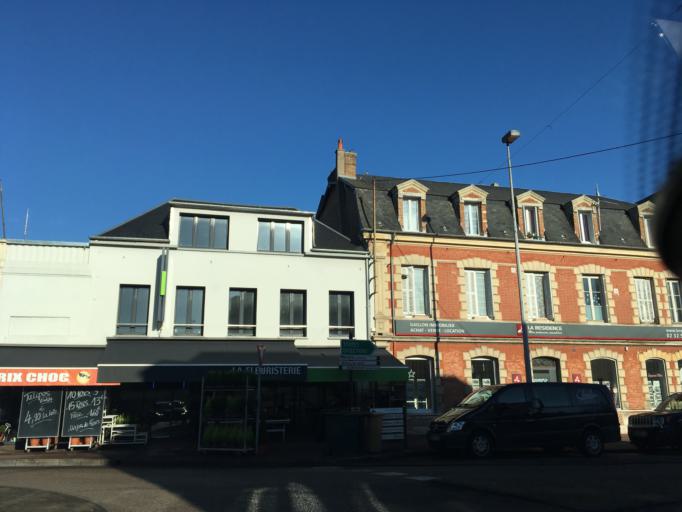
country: FR
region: Haute-Normandie
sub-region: Departement de l'Eure
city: Gaillon
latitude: 49.1602
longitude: 1.3359
